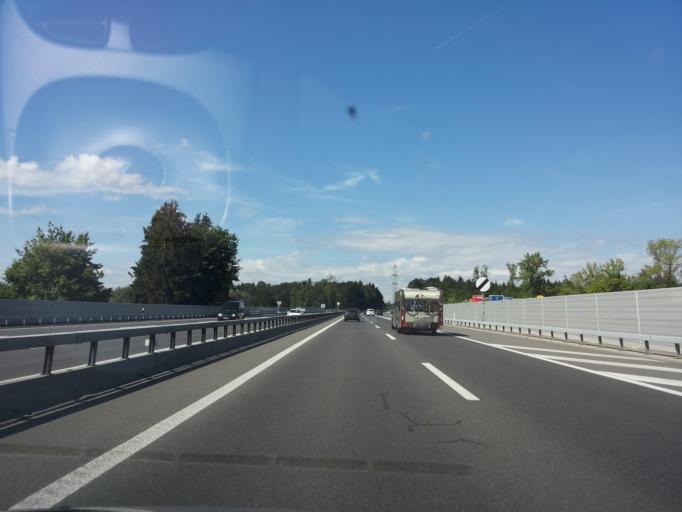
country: CH
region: Lucerne
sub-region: Hochdorf District
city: Emmen
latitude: 47.0887
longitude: 8.2521
